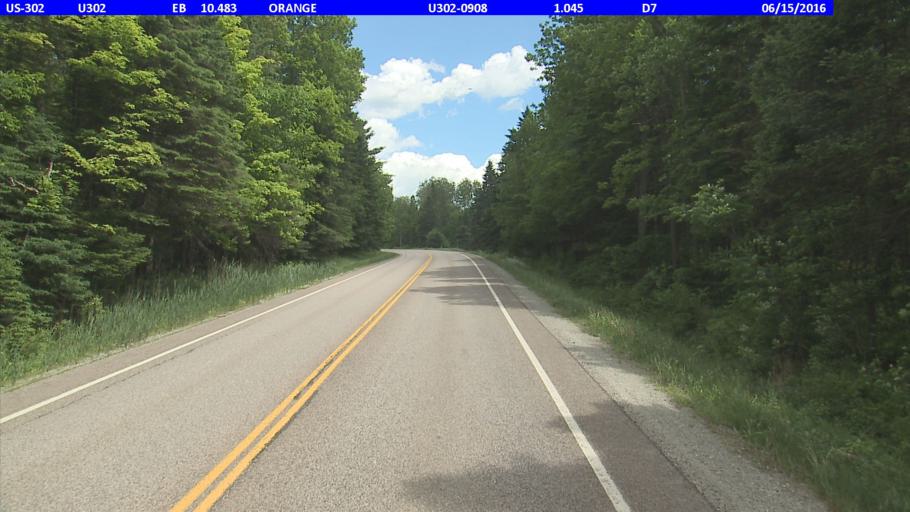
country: US
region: Vermont
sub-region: Washington County
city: South Barre
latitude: 44.1511
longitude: -72.4177
